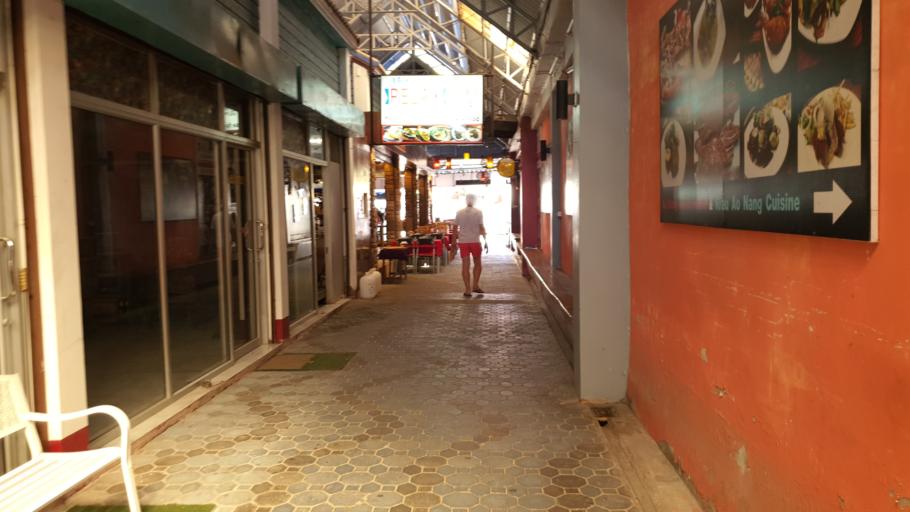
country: TH
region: Phangnga
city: Ban Ao Nang
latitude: 8.0351
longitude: 98.8186
